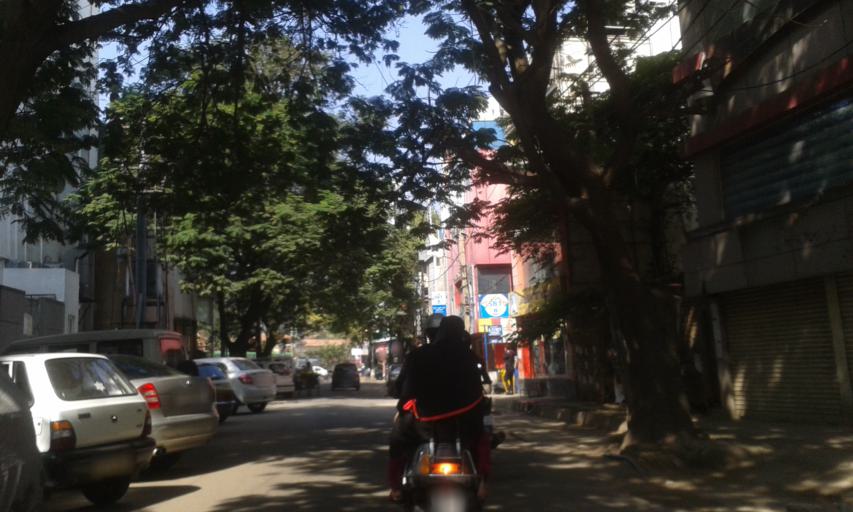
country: IN
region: Karnataka
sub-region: Bangalore Urban
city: Bangalore
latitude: 12.9679
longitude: 77.6071
